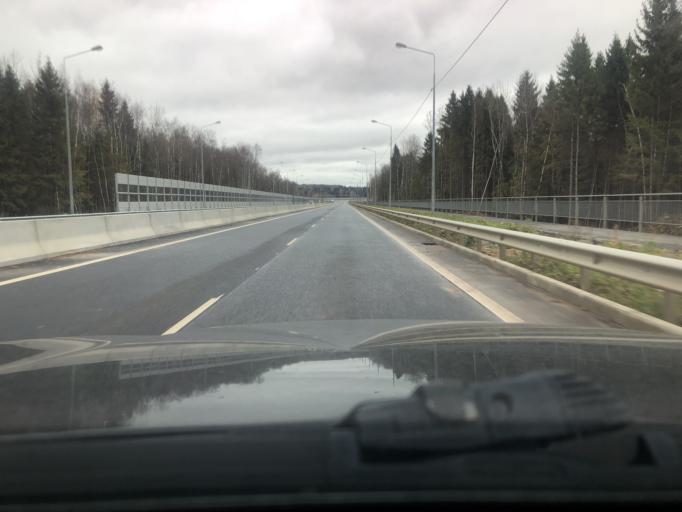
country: RU
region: Moskovskaya
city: Semkhoz
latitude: 56.3339
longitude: 38.0857
